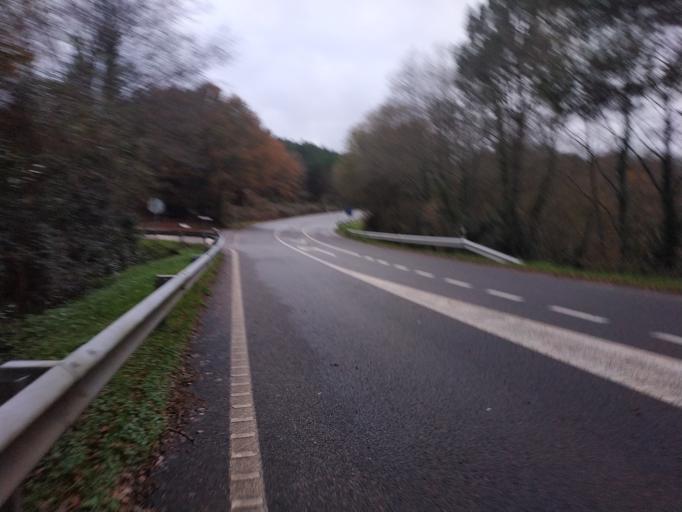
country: ES
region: Galicia
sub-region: Provincia de Pontevedra
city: Silleda
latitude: 42.7790
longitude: -8.1764
